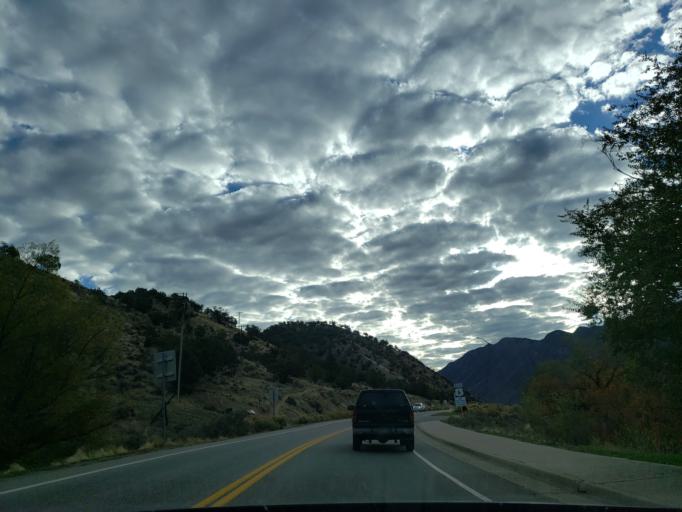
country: US
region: Colorado
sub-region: Garfield County
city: New Castle
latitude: 39.5715
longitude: -107.5258
